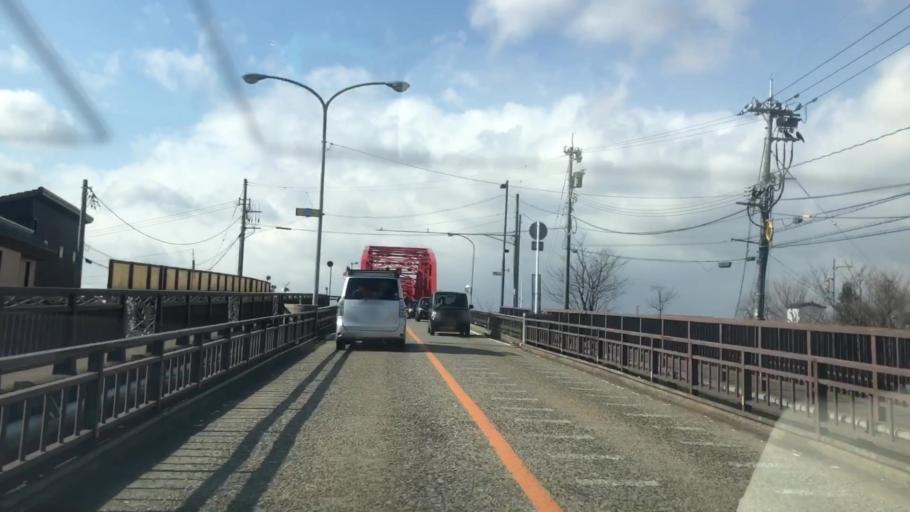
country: JP
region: Toyama
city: Takaoka
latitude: 36.7347
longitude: 137.0454
